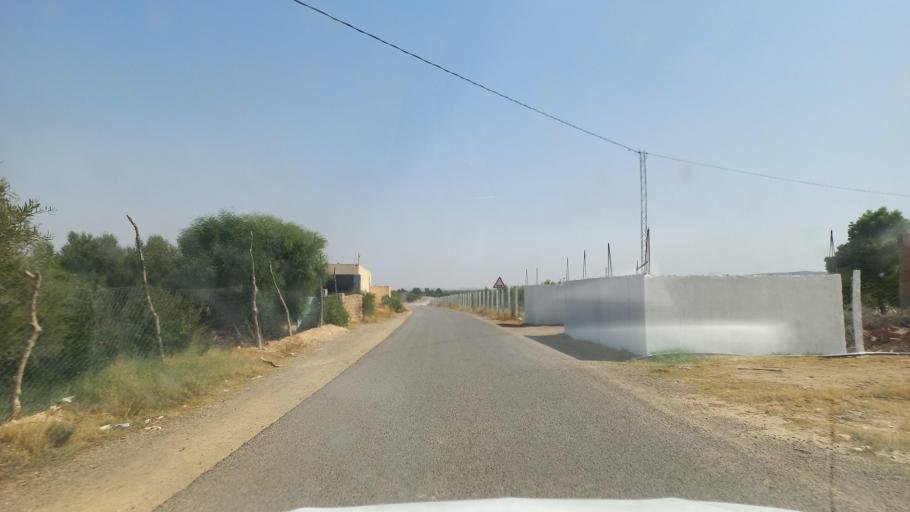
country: TN
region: Al Qasrayn
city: Kasserine
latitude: 35.2436
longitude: 9.0267
